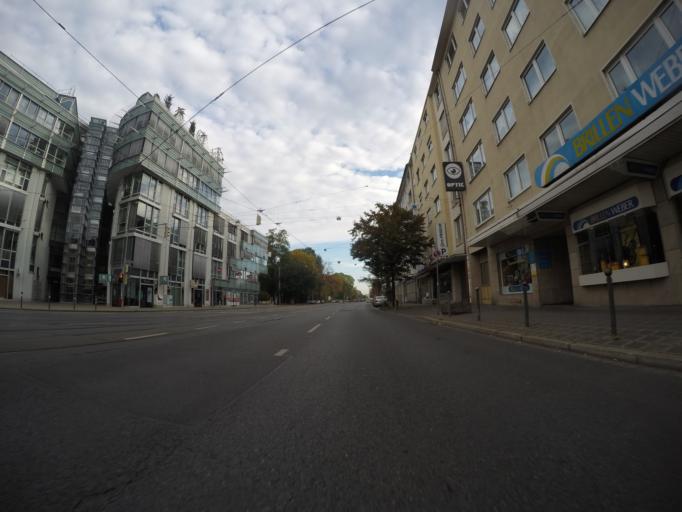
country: DE
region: Bavaria
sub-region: Regierungsbezirk Mittelfranken
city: Nuernberg
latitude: 49.4623
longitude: 11.0934
